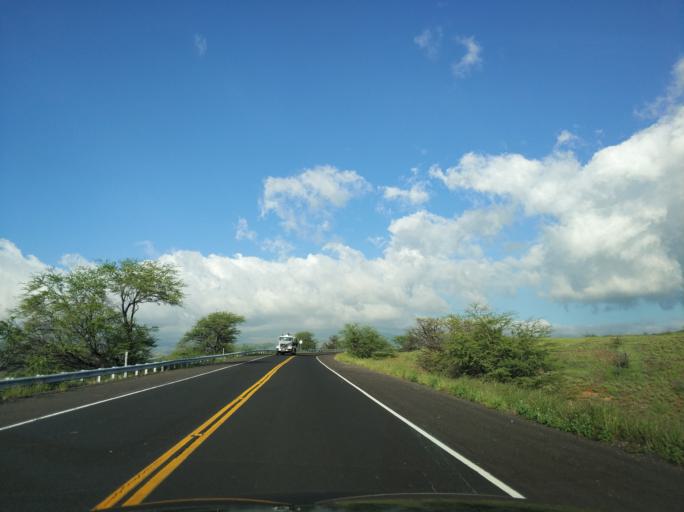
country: US
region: Hawaii
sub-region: Hawaii County
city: Waikoloa Village
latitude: 19.9753
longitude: -155.8263
